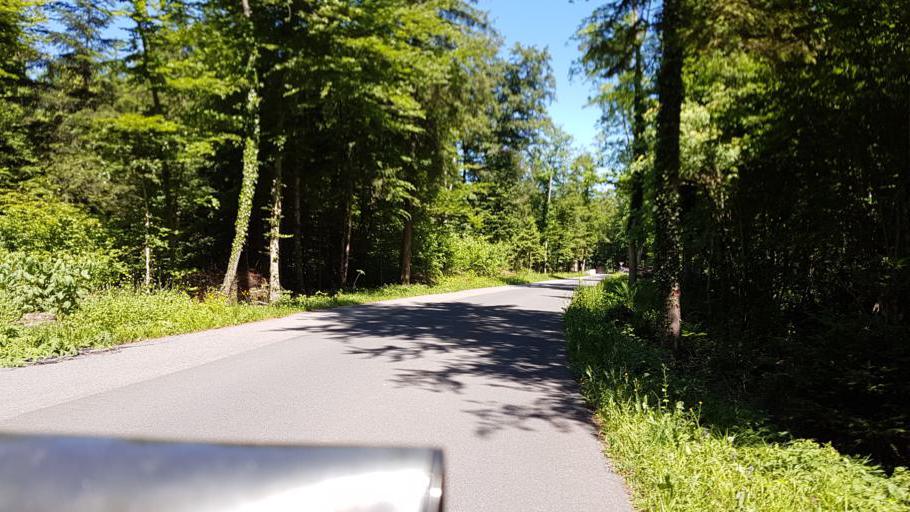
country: CH
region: Bern
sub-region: Thun District
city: Thierachern
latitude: 46.7335
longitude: 7.5865
